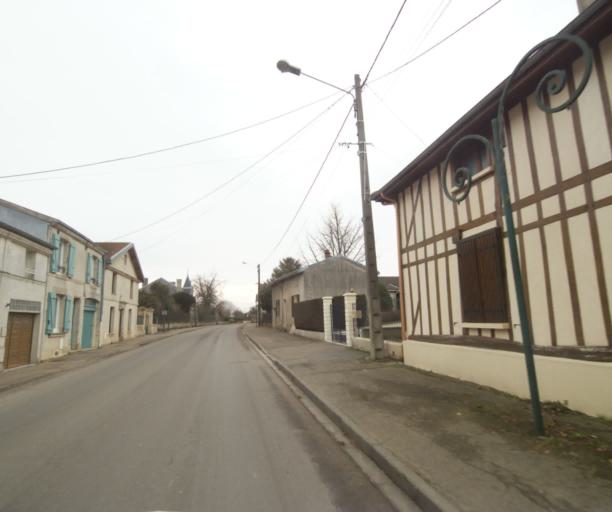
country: FR
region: Champagne-Ardenne
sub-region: Departement de la Haute-Marne
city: Villiers-en-Lieu
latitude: 48.6657
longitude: 4.9028
